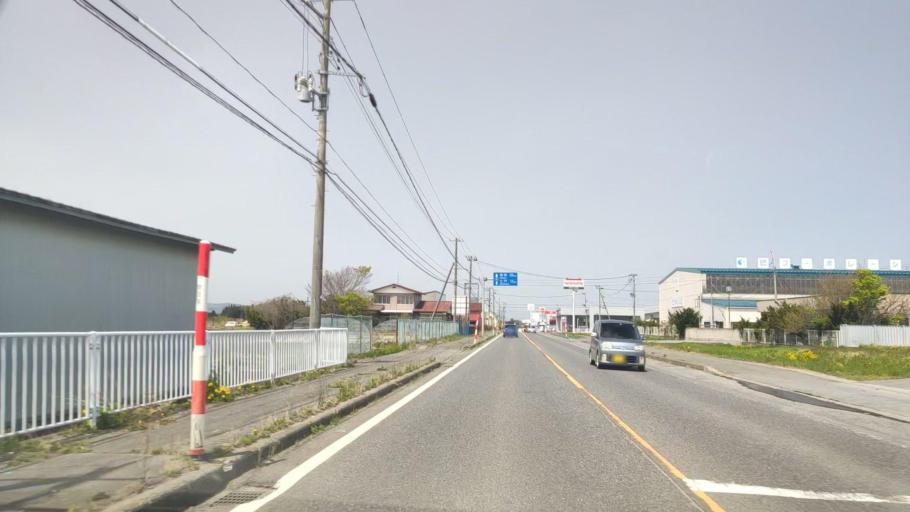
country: JP
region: Aomori
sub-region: Misawa Shi
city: Inuotose
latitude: 40.6481
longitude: 141.1971
